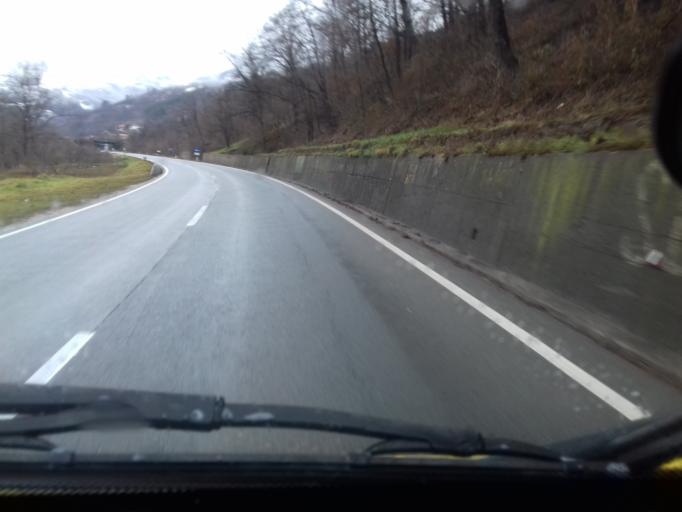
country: BA
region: Federation of Bosnia and Herzegovina
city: Zeljezno Polje
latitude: 44.3565
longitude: 17.9563
